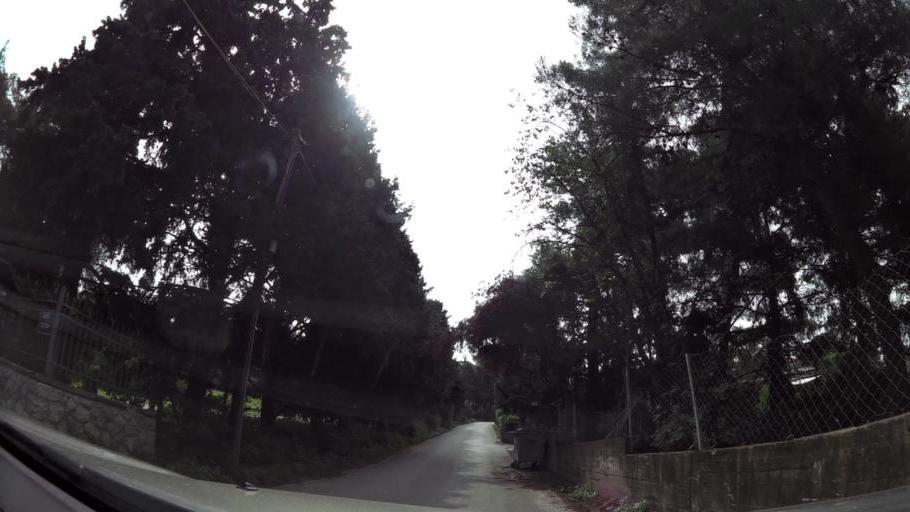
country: GR
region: Central Macedonia
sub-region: Nomos Thessalonikis
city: Panorama
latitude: 40.5905
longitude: 23.0127
